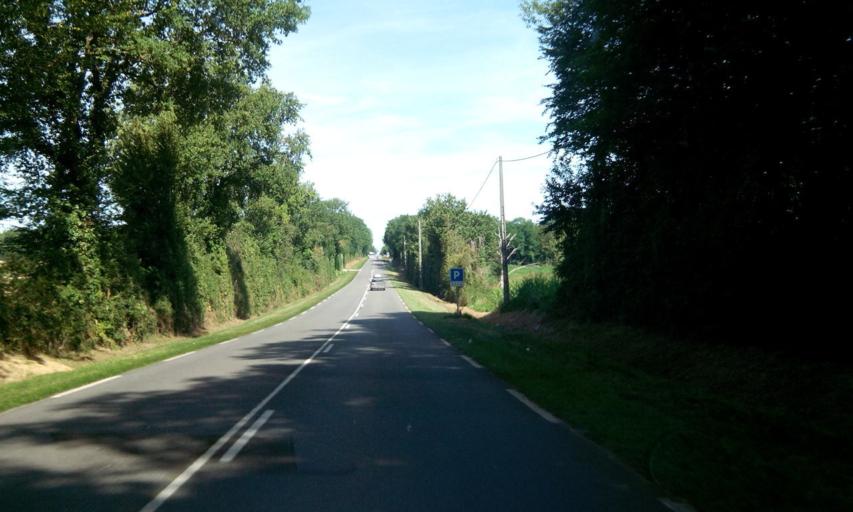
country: FR
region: Poitou-Charentes
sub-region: Departement de la Charente
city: Confolens
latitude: 45.9837
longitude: 0.6792
